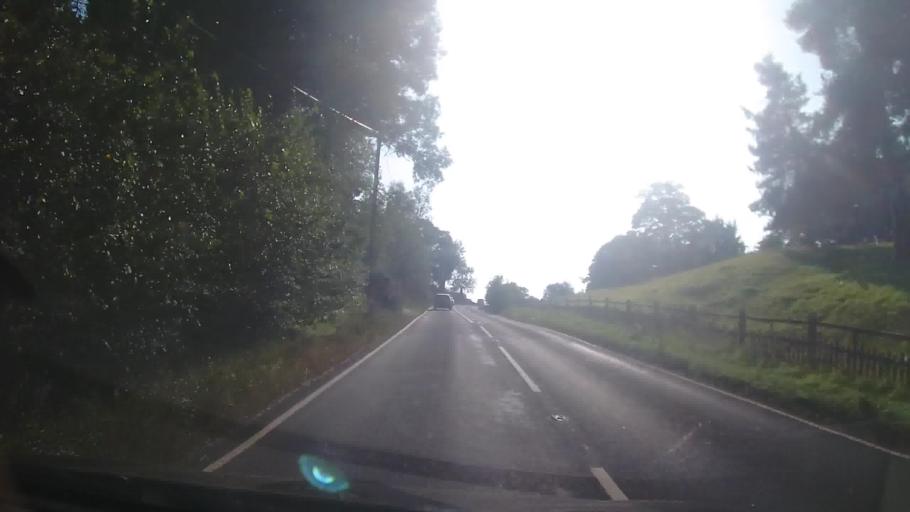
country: GB
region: England
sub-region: Shropshire
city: Alveley
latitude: 52.4999
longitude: -2.3736
